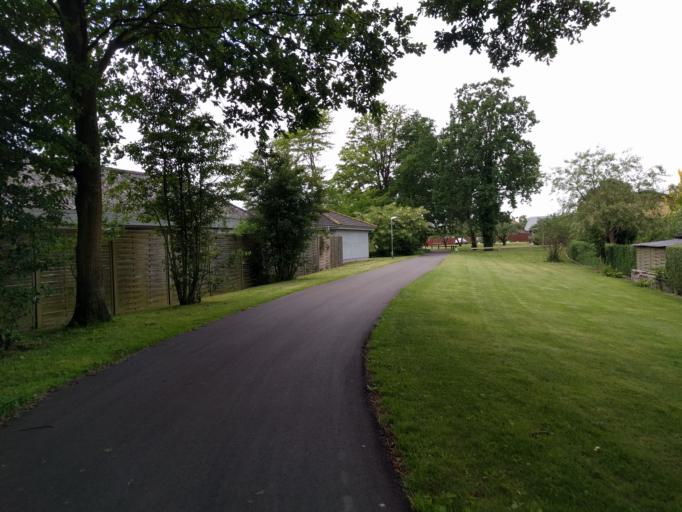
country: DK
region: South Denmark
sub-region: Odense Kommune
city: Bullerup
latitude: 55.4256
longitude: 10.4736
